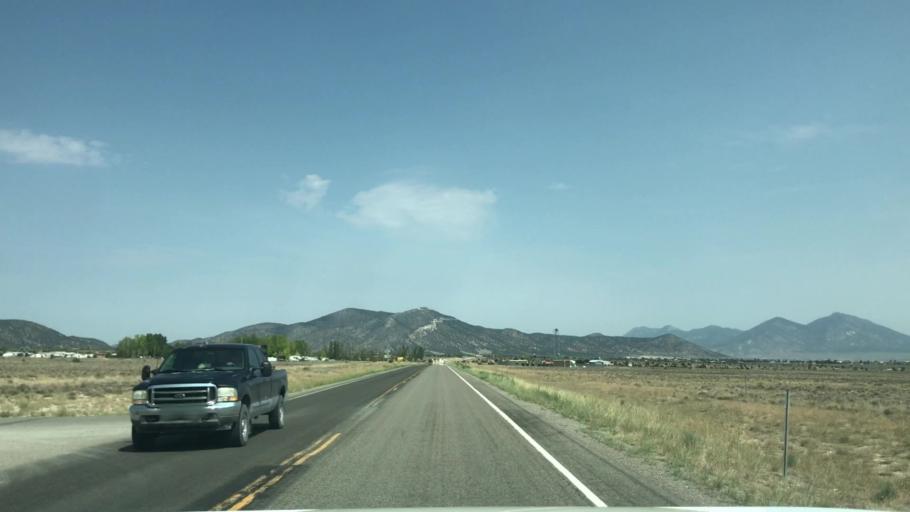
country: US
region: Nevada
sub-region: White Pine County
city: Ely
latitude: 39.2088
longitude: -114.8490
